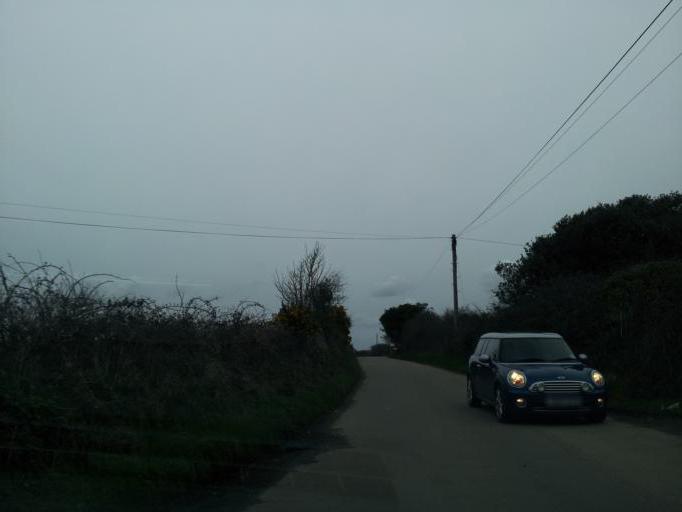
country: GB
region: England
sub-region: Cornwall
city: St. Day
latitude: 50.2634
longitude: -5.1954
